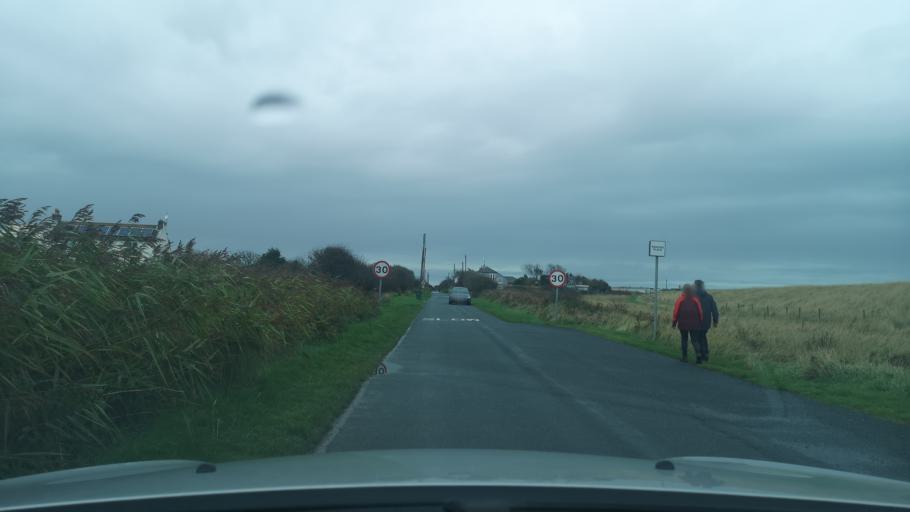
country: GB
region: England
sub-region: East Riding of Yorkshire
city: Easington
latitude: 53.6185
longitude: 0.1397
